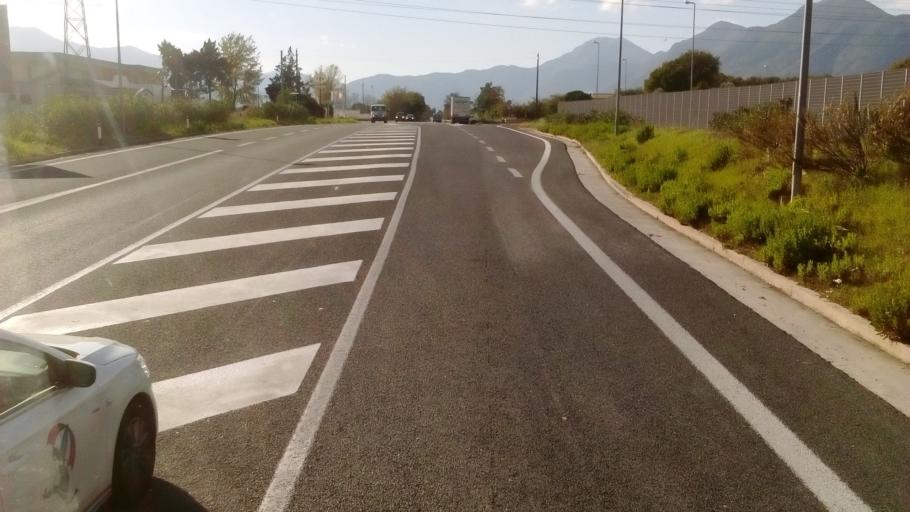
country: IT
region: Molise
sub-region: Provincia di Isernia
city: Taverna Ravindola
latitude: 41.5080
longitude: 14.1111
